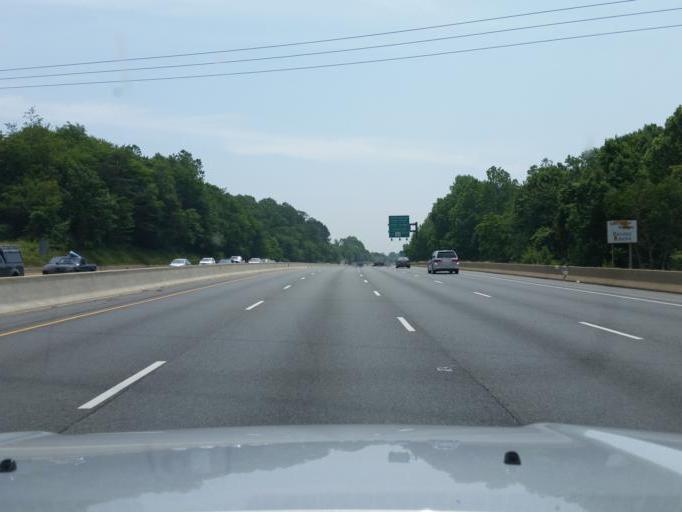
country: US
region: Maryland
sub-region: Montgomery County
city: Gaithersburg
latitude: 39.1597
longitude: -77.2304
